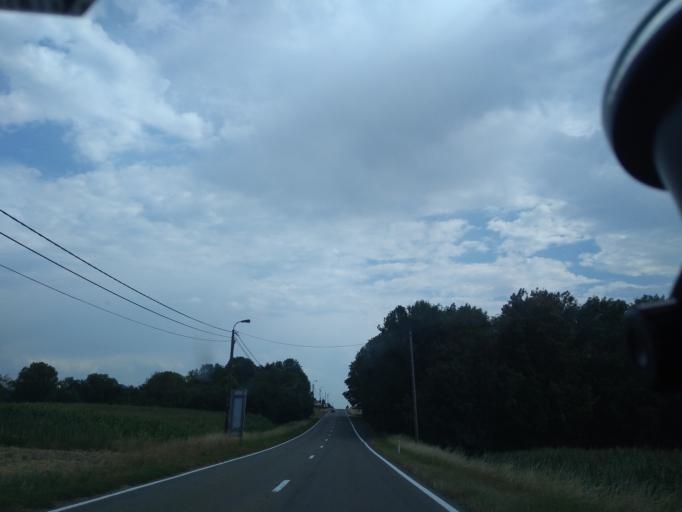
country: BE
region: Wallonia
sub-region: Province de Namur
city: Beauraing
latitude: 50.1594
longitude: 4.9152
